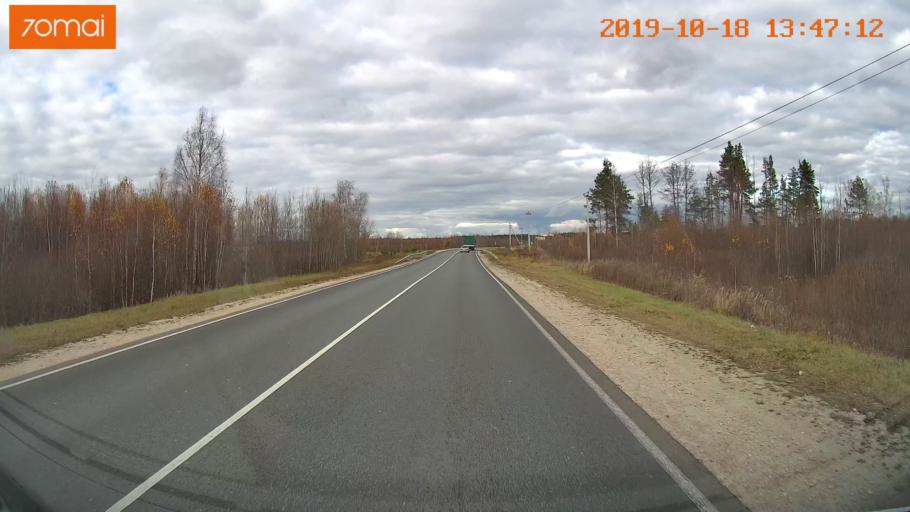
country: RU
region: Rjazan
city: Solotcha
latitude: 54.9712
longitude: 39.9514
